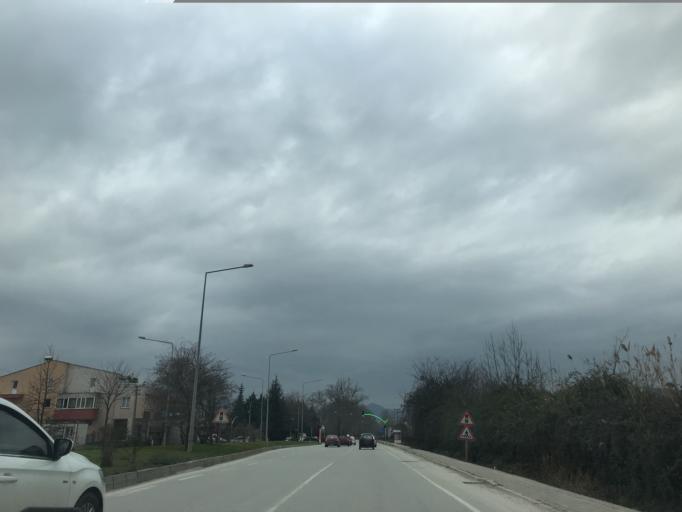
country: TR
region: Yalova
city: Yalova
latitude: 40.6514
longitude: 29.2423
